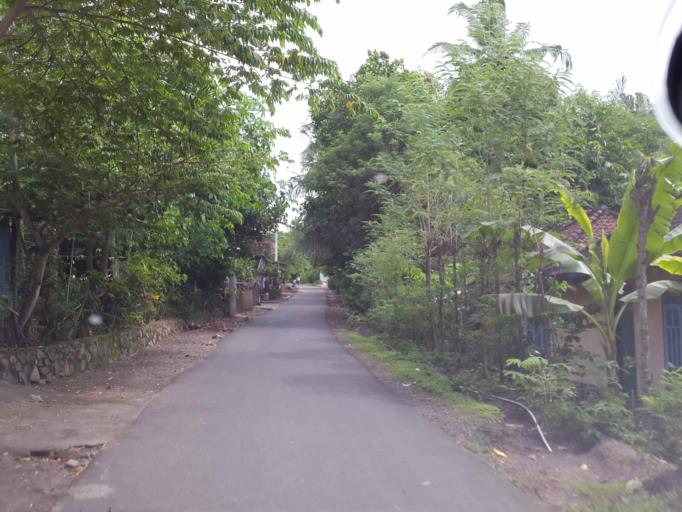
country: ID
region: West Nusa Tenggara
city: Dasangeria Selatan
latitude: -8.5417
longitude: 116.1513
